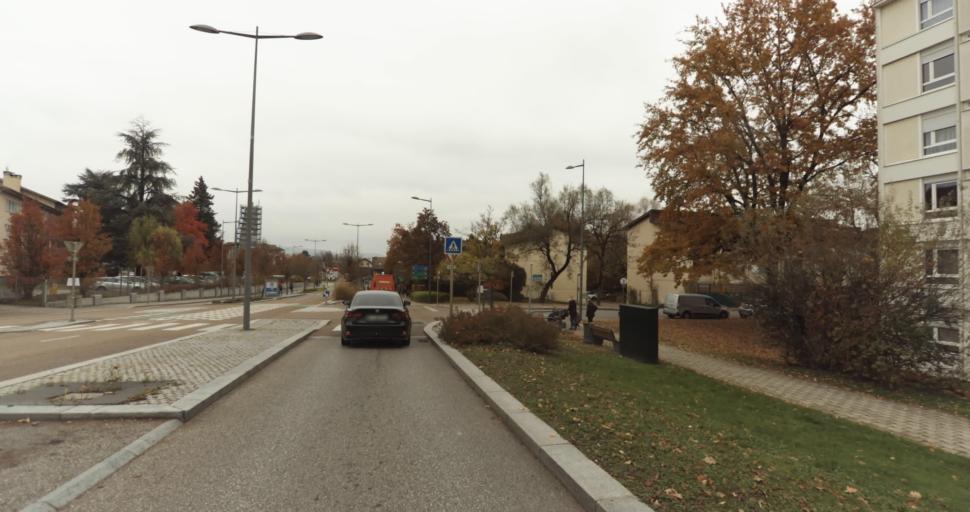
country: FR
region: Rhone-Alpes
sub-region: Departement de la Haute-Savoie
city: Cran-Gevrier
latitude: 45.8921
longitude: 6.1016
